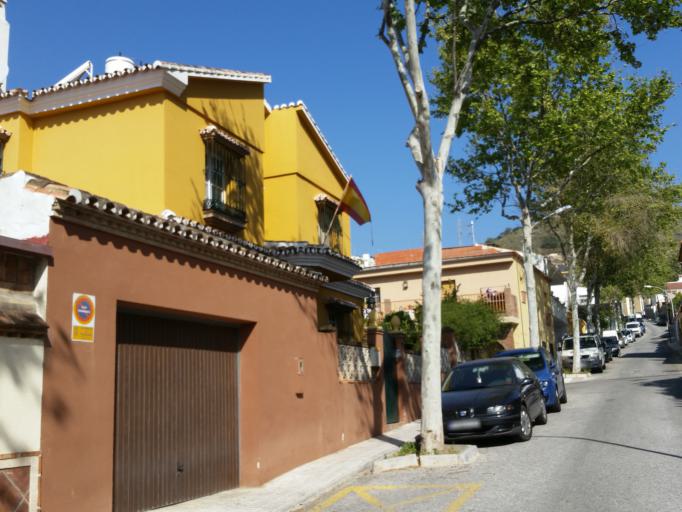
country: ES
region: Andalusia
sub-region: Provincia de Malaga
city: Benalmadena
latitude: 36.6072
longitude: -4.5366
